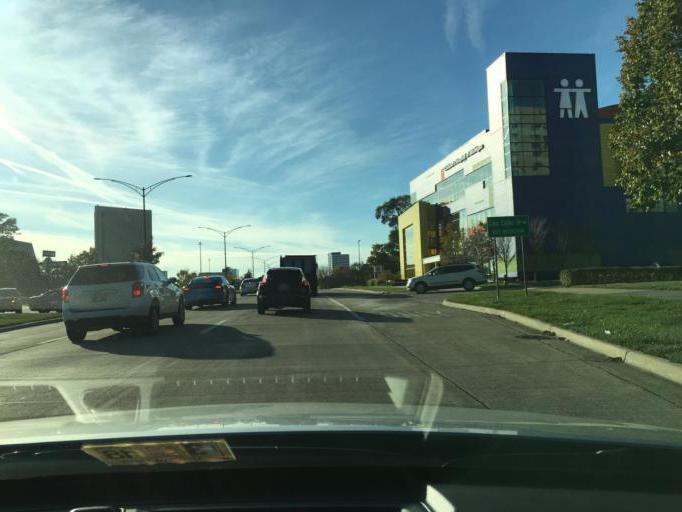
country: US
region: Michigan
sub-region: Oakland County
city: Clawson
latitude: 42.5625
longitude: -83.1520
